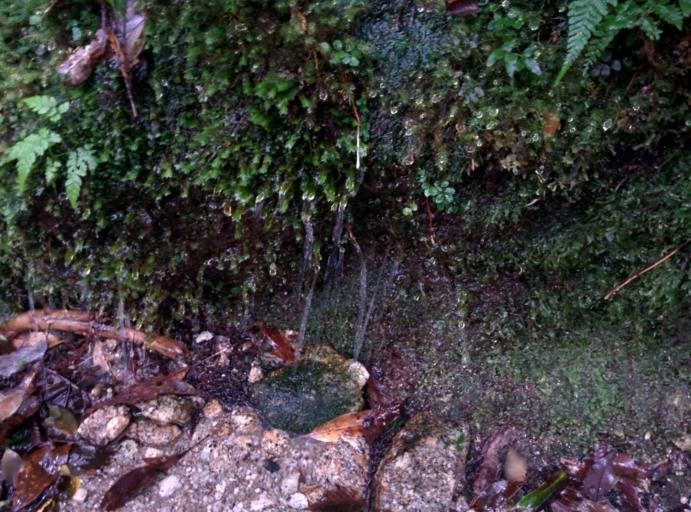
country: JP
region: Kagoshima
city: Nishinoomote
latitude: 30.3723
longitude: 130.5705
